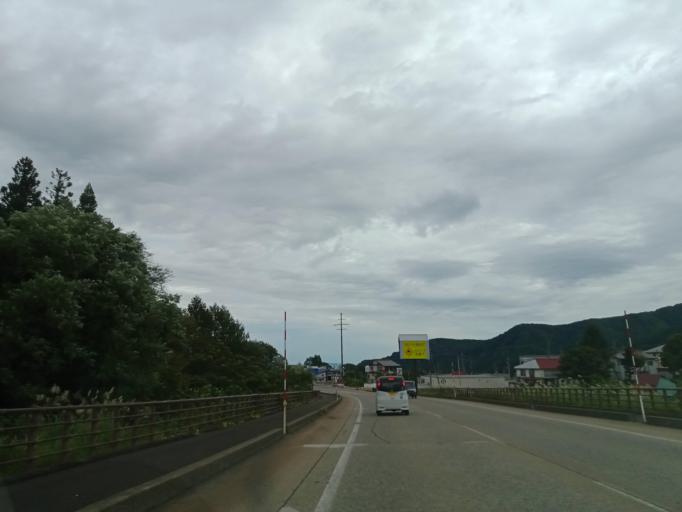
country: JP
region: Niigata
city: Arai
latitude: 36.8760
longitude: 138.2032
